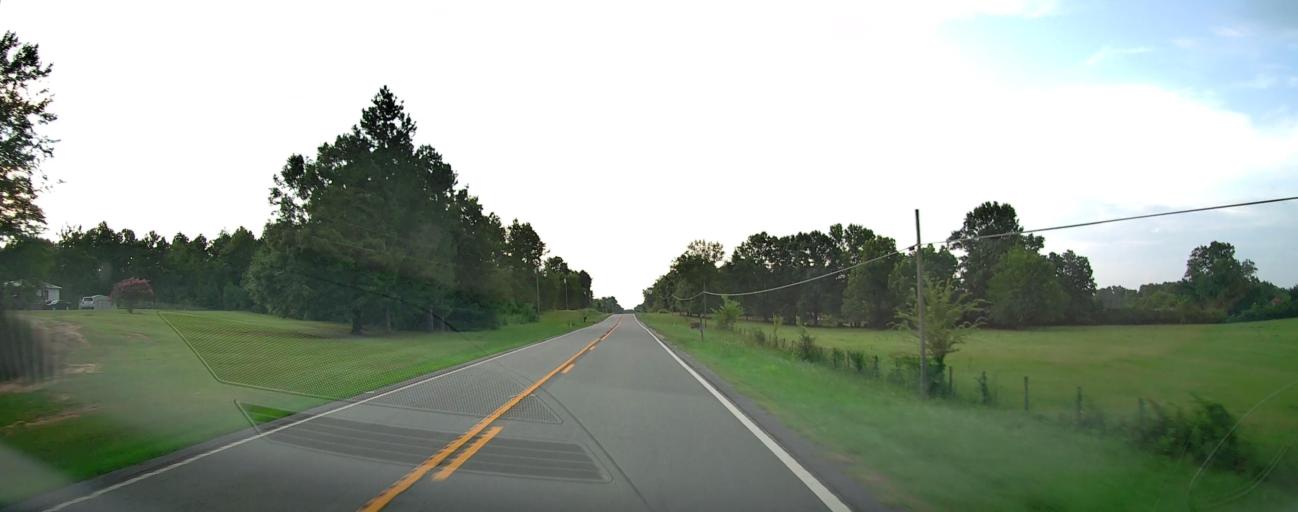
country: US
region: Georgia
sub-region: Taylor County
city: Reynolds
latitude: 32.6018
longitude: -84.0946
